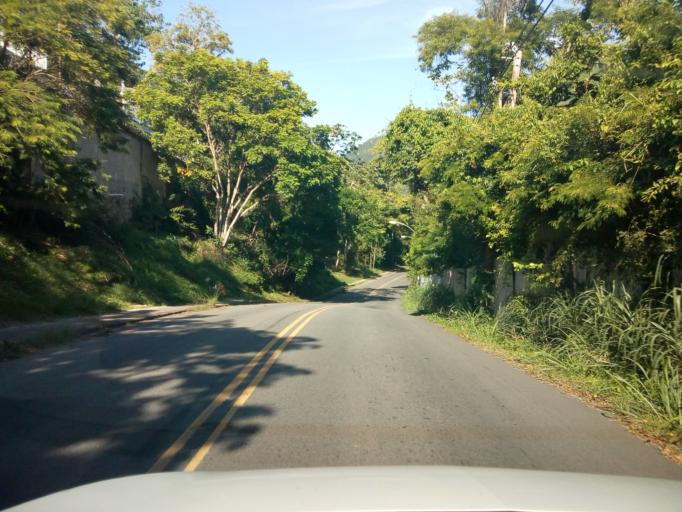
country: BR
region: Rio de Janeiro
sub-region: Nilopolis
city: Nilopolis
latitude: -23.0256
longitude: -43.5052
